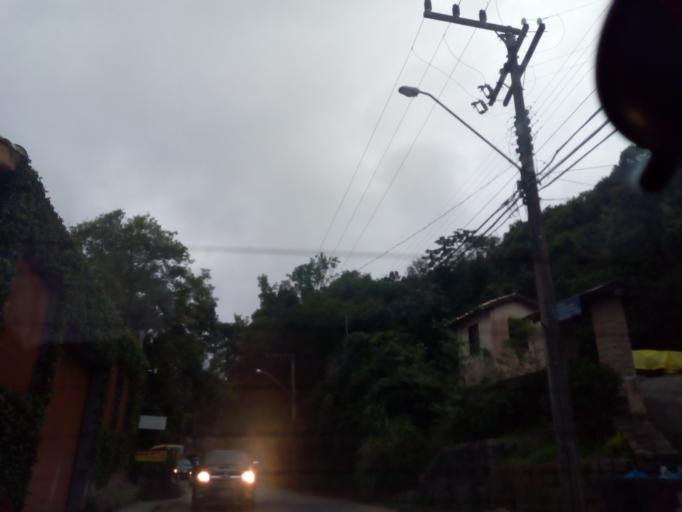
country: BR
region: Santa Catarina
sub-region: Florianopolis
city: Itacorubi
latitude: -27.3914
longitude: -48.4207
